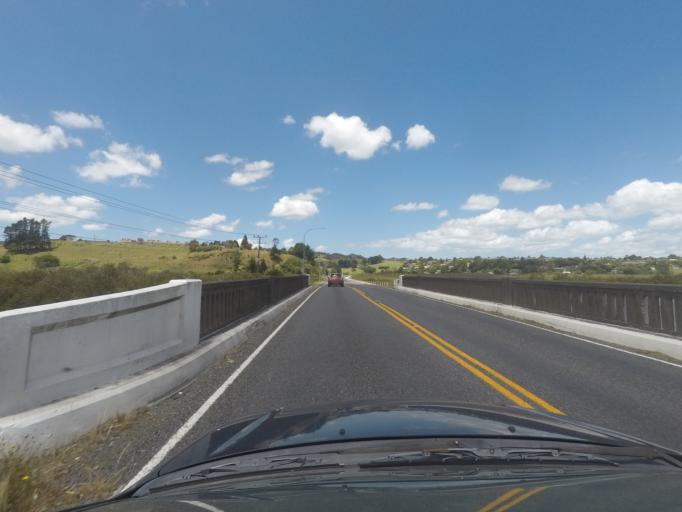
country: NZ
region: Northland
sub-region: Whangarei
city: Whangarei
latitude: -35.7374
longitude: 174.3554
